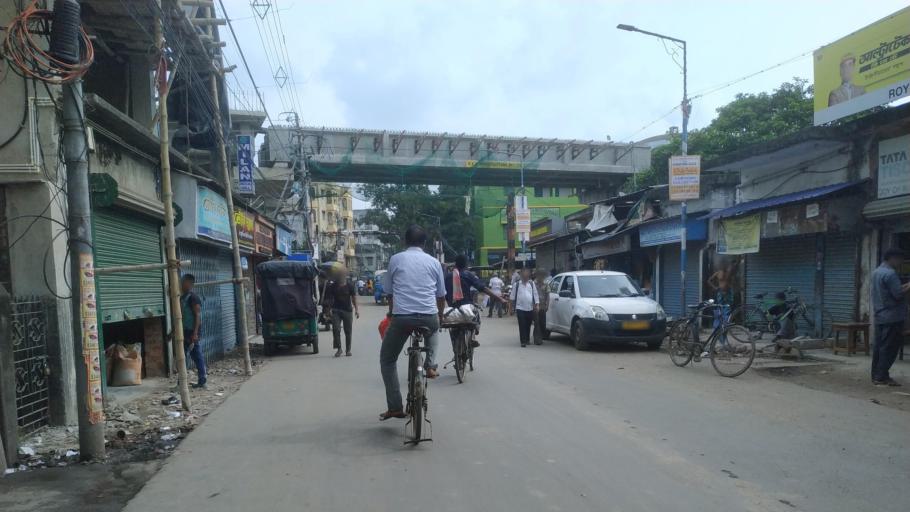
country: IN
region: West Bengal
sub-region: North 24 Parganas
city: Dam Dam
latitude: 22.6394
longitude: 88.4155
